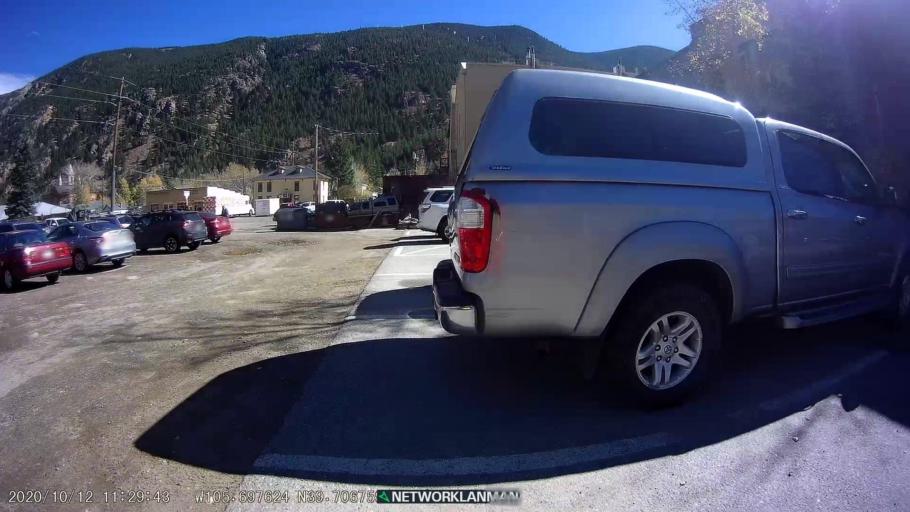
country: US
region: Colorado
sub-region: Clear Creek County
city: Georgetown
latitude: 39.7068
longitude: -105.6977
